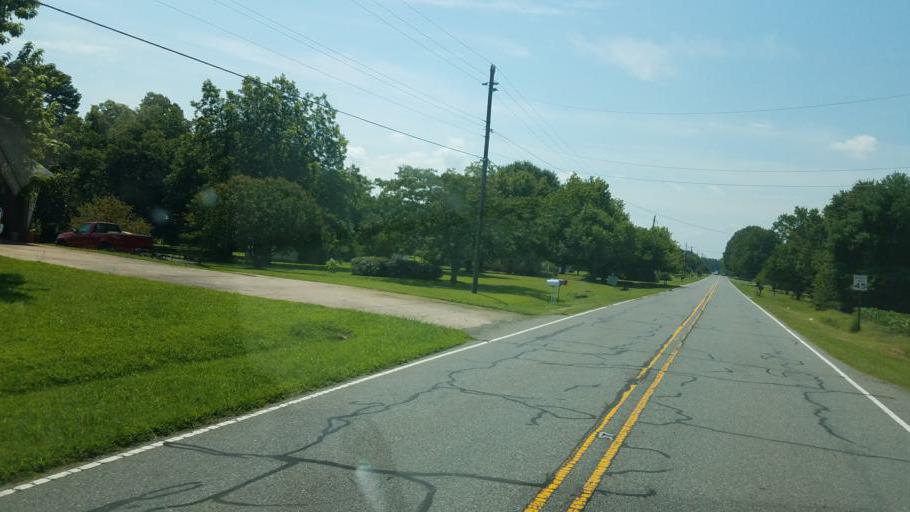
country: US
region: North Carolina
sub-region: Gaston County
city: Cherryville
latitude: 35.5033
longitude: -81.4565
